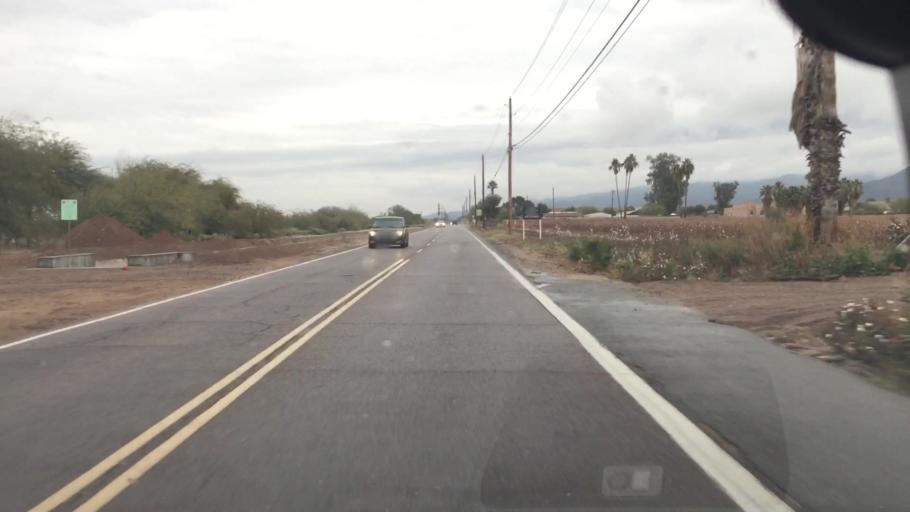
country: US
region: Arizona
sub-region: Maricopa County
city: Laveen
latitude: 33.3630
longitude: -112.1435
